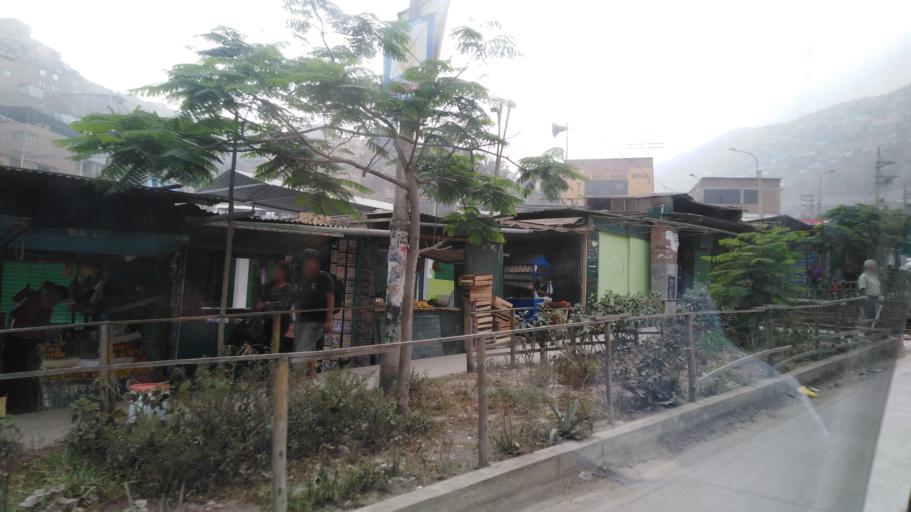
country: PE
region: Lima
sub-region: Lima
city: La Molina
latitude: -12.1472
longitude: -76.9349
